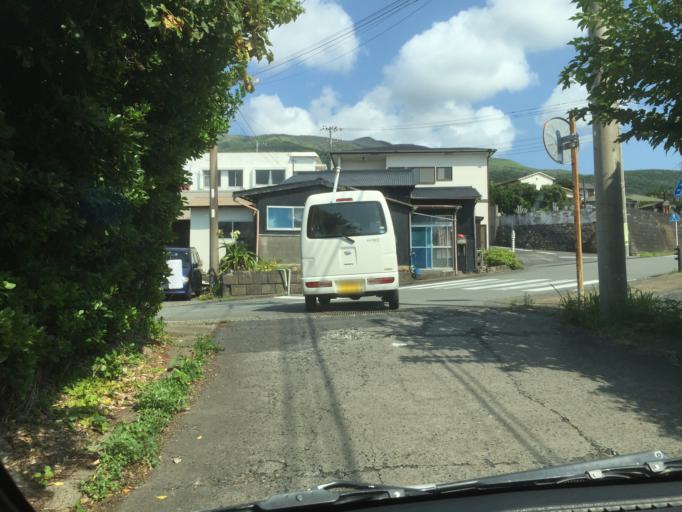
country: JP
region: Shizuoka
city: Shimoda
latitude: 34.0593
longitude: 139.5464
